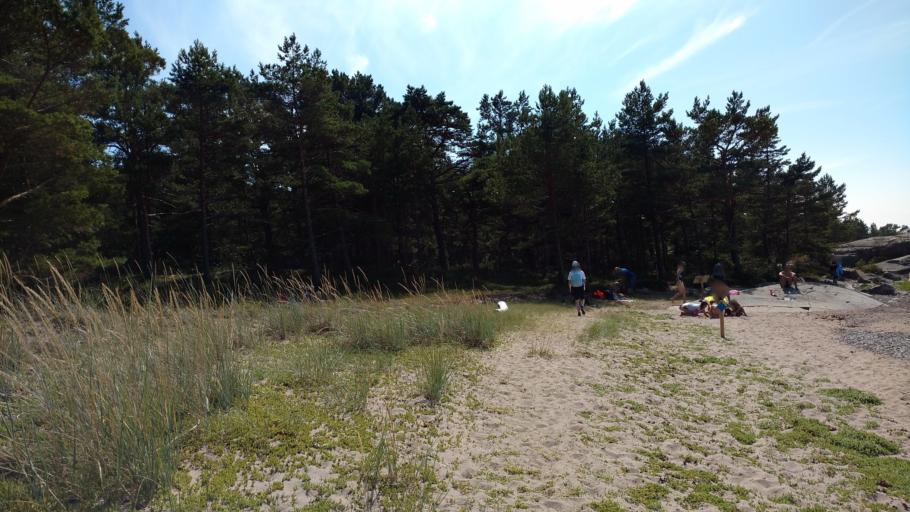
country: FI
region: Varsinais-Suomi
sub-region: Aboland-Turunmaa
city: Dragsfjaerd
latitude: 59.8067
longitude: 22.3134
